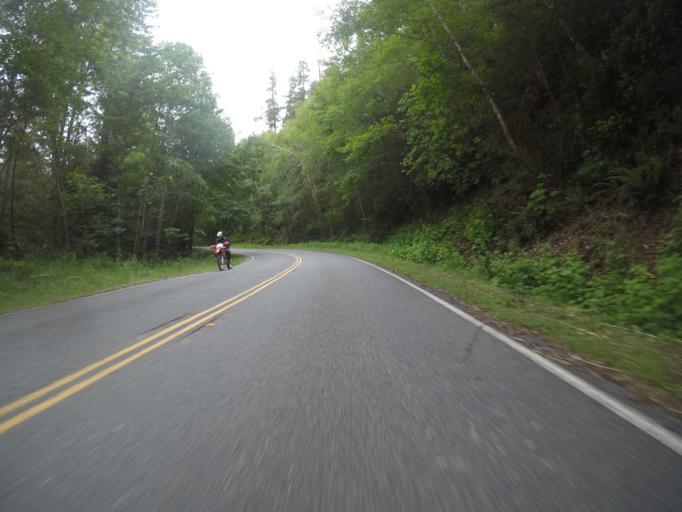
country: US
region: California
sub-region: Del Norte County
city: Bertsch-Oceanview
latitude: 41.7676
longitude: -124.0103
